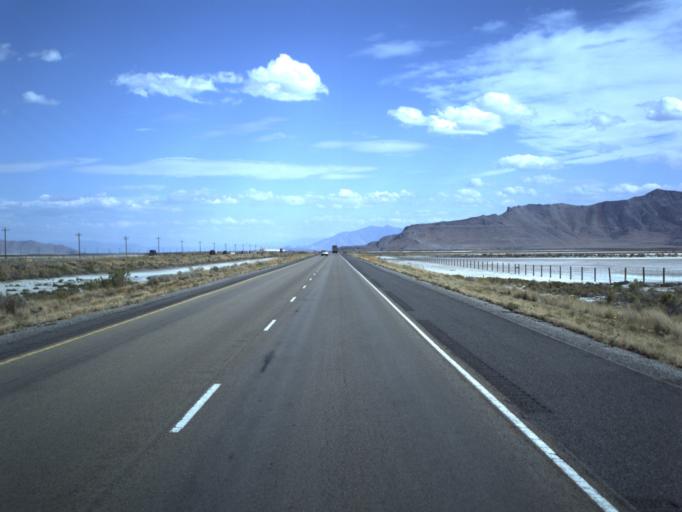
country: US
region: Utah
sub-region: Tooele County
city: Grantsville
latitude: 40.7532
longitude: -112.7287
